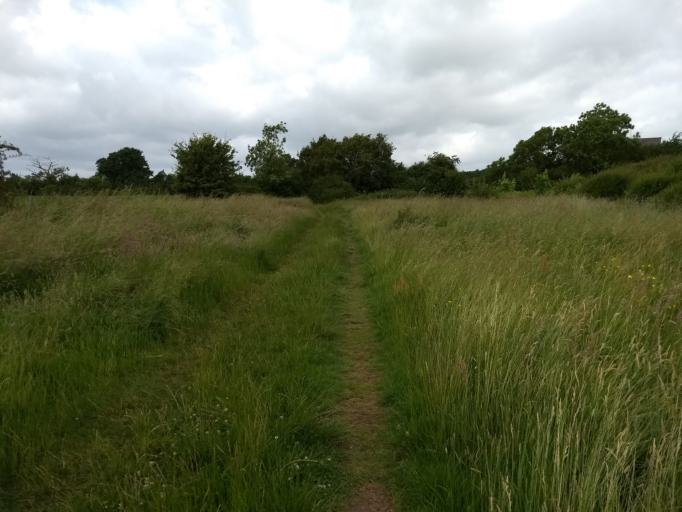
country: GB
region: England
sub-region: Milton Keynes
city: Shenley Church End
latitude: 52.0055
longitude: -0.8116
